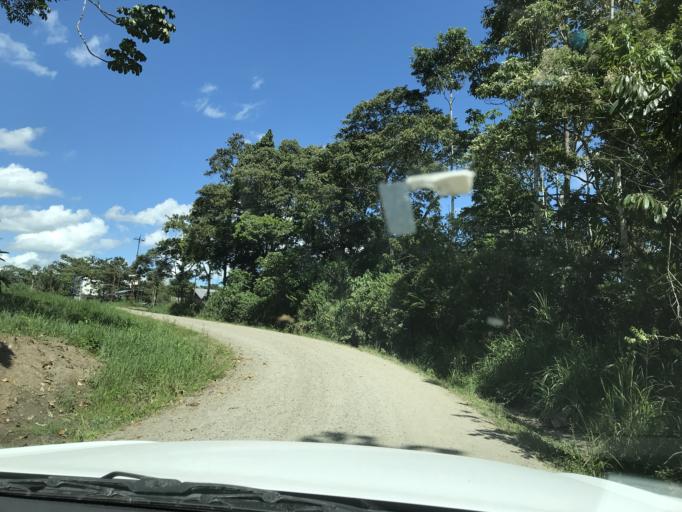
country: EC
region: Orellana
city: Puerto Francisco de Orellana
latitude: -0.4458
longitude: -76.6084
